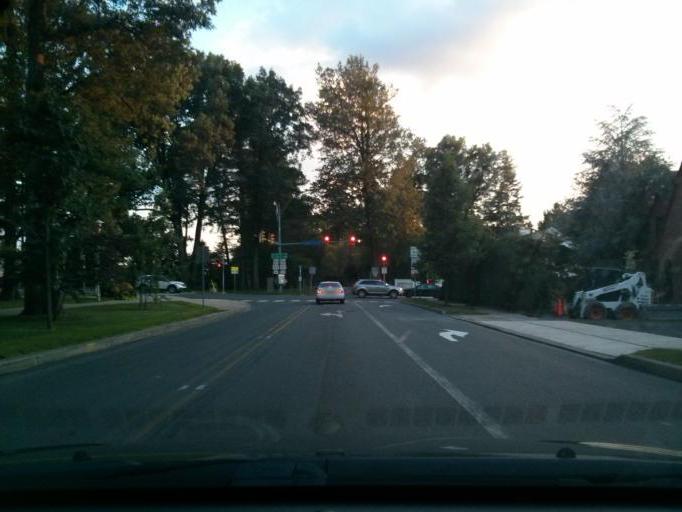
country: US
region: Pennsylvania
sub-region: Centre County
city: State College
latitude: 40.7972
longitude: -77.8720
